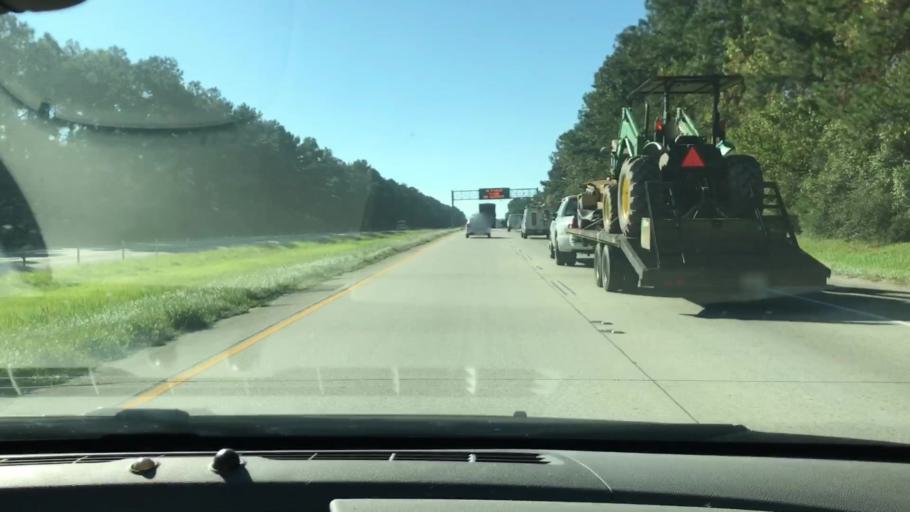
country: US
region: Louisiana
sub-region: Saint Tammany Parish
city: Pearl River
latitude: 30.3342
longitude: -89.7379
